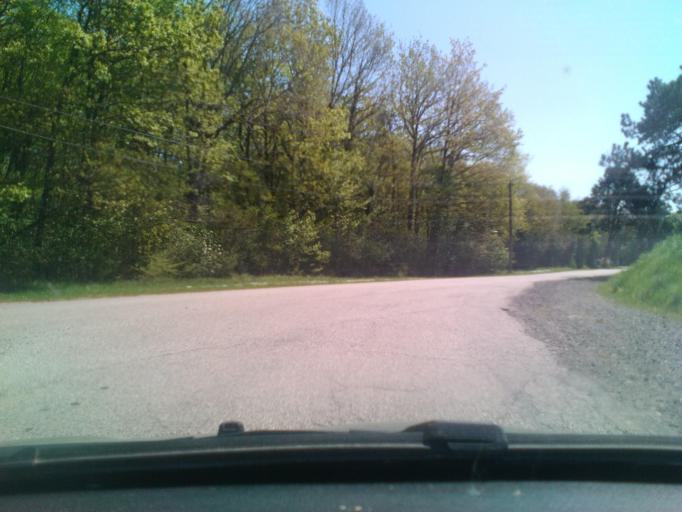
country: FR
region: Lorraine
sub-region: Departement de Meurthe-et-Moselle
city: Ludres
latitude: 48.6299
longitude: 6.1582
